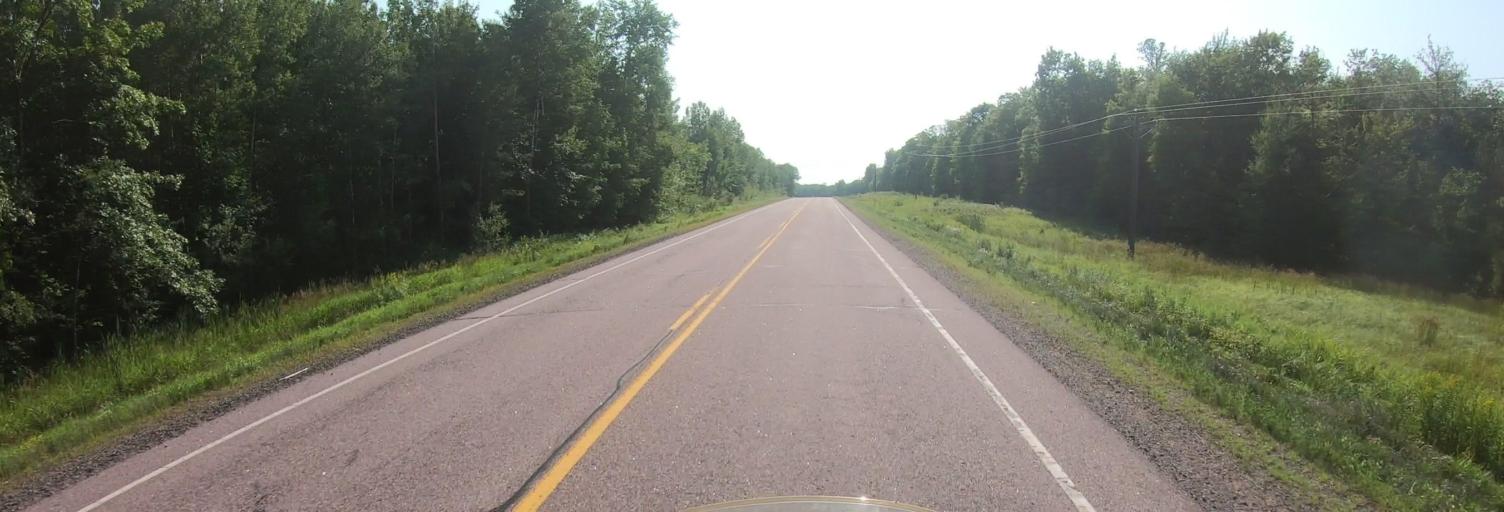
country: US
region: Wisconsin
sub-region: Iron County
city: Hurley
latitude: 46.3558
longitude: -90.4675
